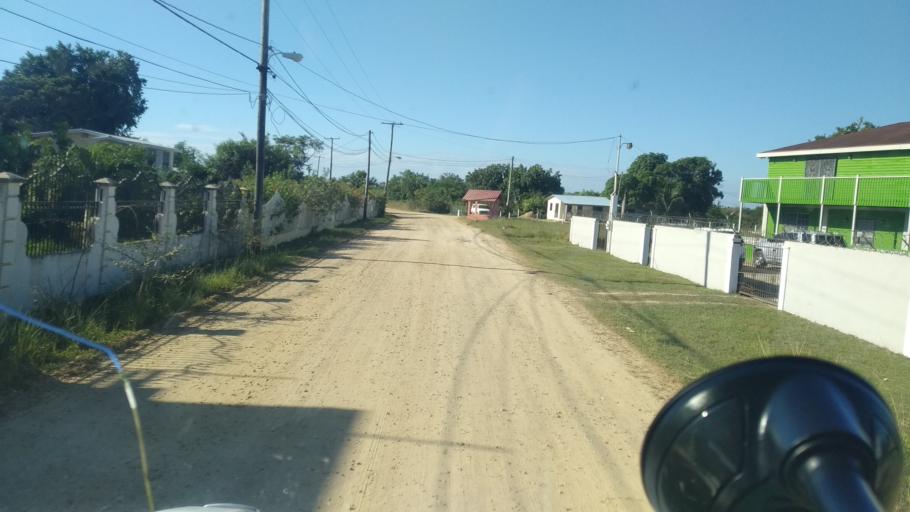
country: BZ
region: Belize
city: Belize City
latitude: 17.5621
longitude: -88.3264
